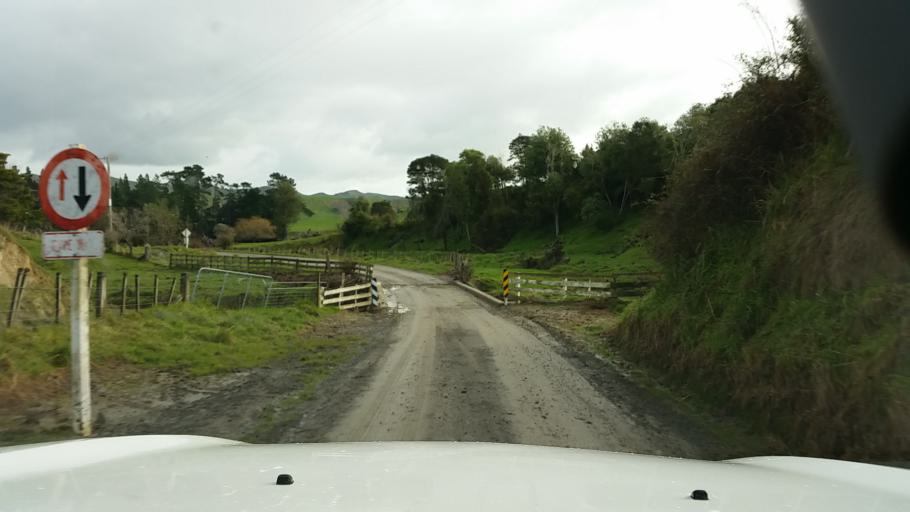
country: NZ
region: Wellington
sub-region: South Wairarapa District
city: Waipawa
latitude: -41.2151
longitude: 175.6003
